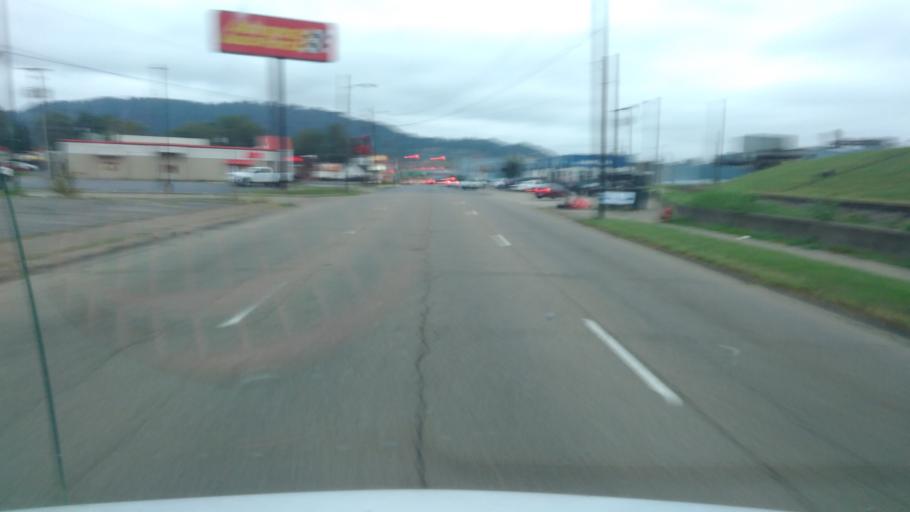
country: US
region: Ohio
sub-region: Scioto County
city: Portsmouth
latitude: 38.7413
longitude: -82.9948
